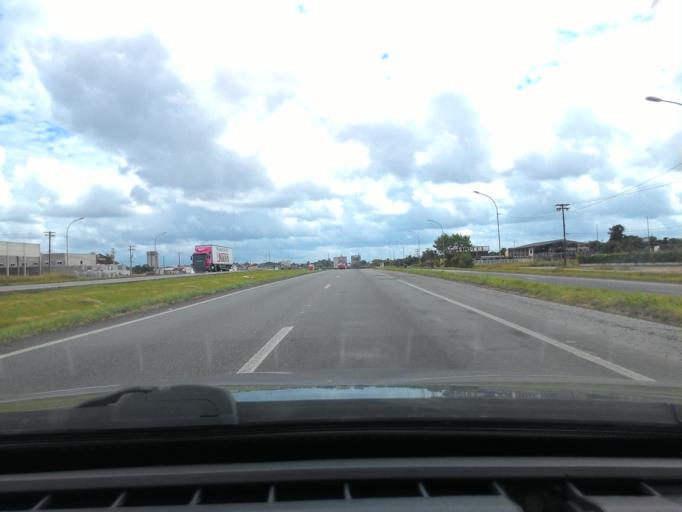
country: BR
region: Sao Paulo
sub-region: Registro
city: Registro
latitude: -24.5161
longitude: -47.8517
